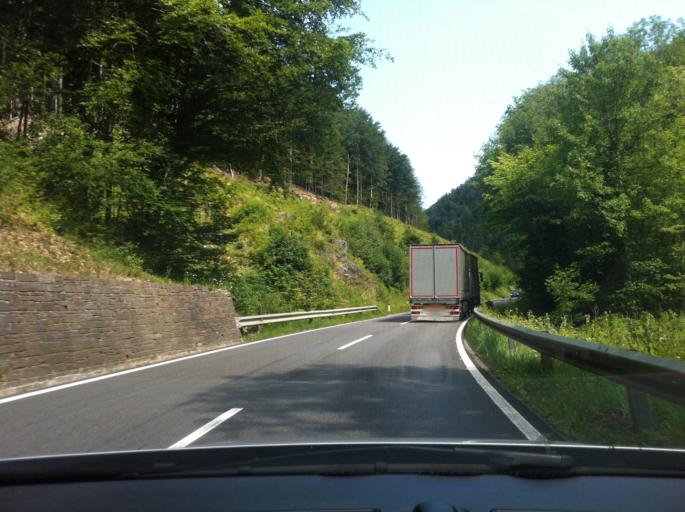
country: AT
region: Styria
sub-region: Politischer Bezirk Weiz
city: Floing
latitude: 47.2444
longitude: 15.7688
